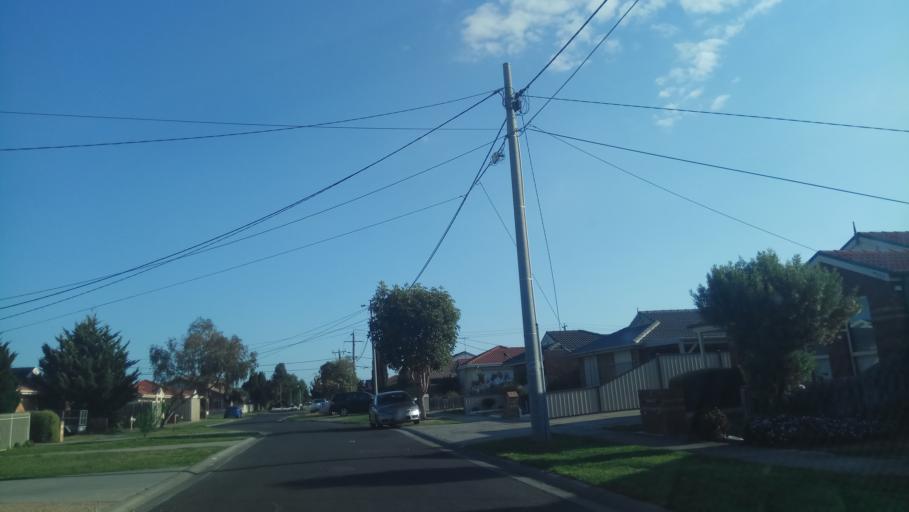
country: AU
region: Victoria
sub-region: Hobsons Bay
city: Altona Meadows
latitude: -37.8734
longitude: 144.7795
